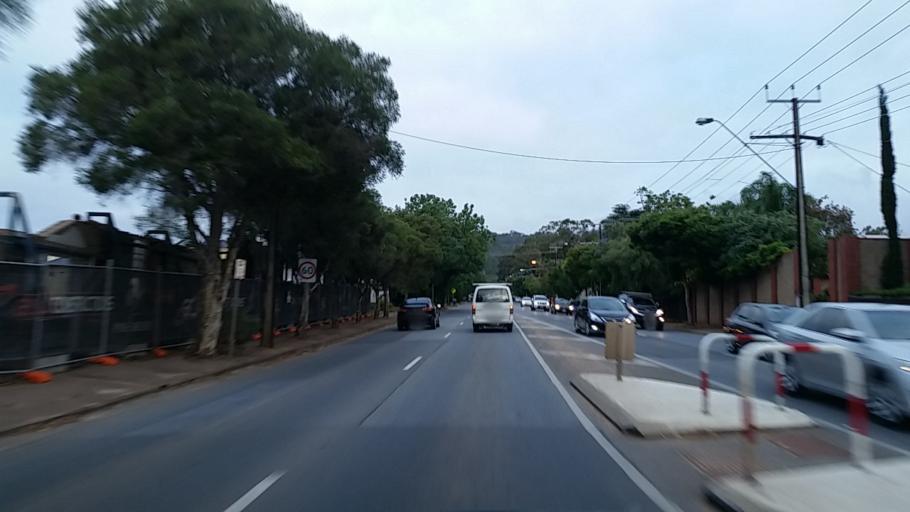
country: AU
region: South Australia
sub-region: Burnside
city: Glenunga
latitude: -34.9641
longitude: 138.6356
